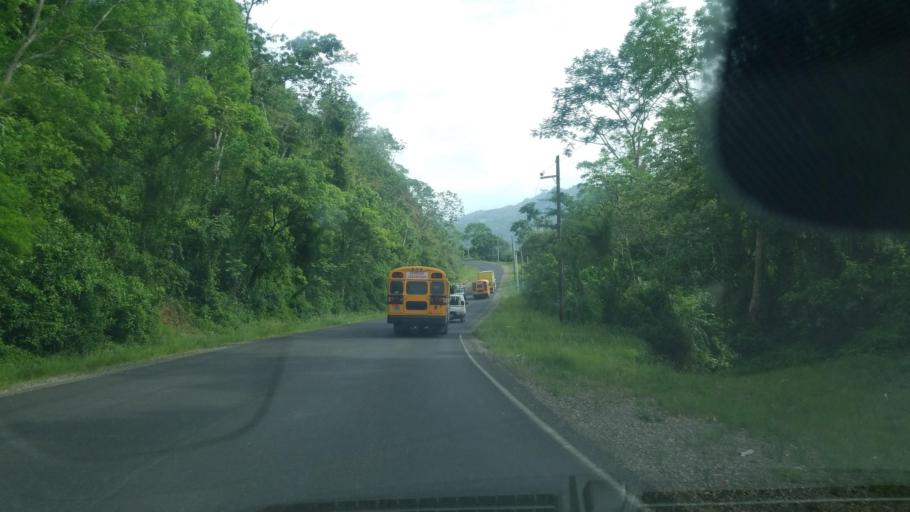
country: HN
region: Santa Barbara
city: Petoa
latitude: 15.2149
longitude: -88.2696
